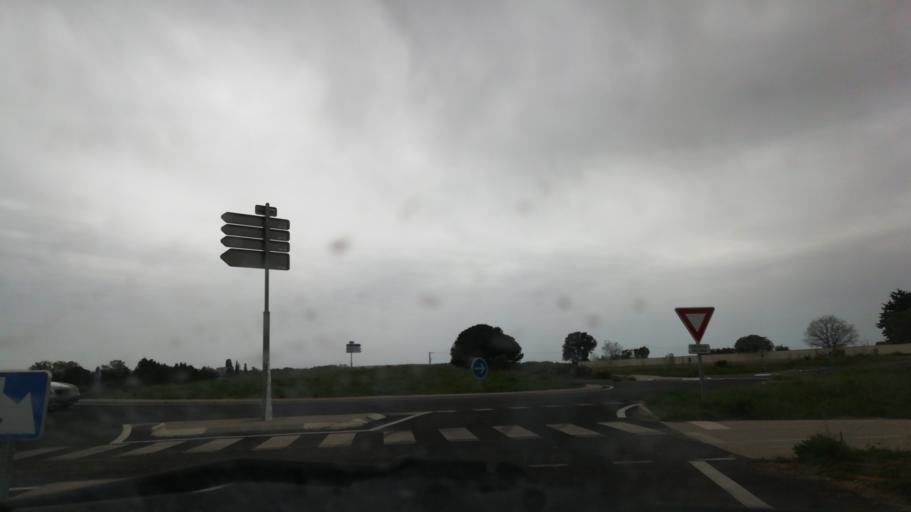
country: FR
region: Languedoc-Roussillon
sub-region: Departement de l'Herault
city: Aniane
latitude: 43.6832
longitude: 3.5762
